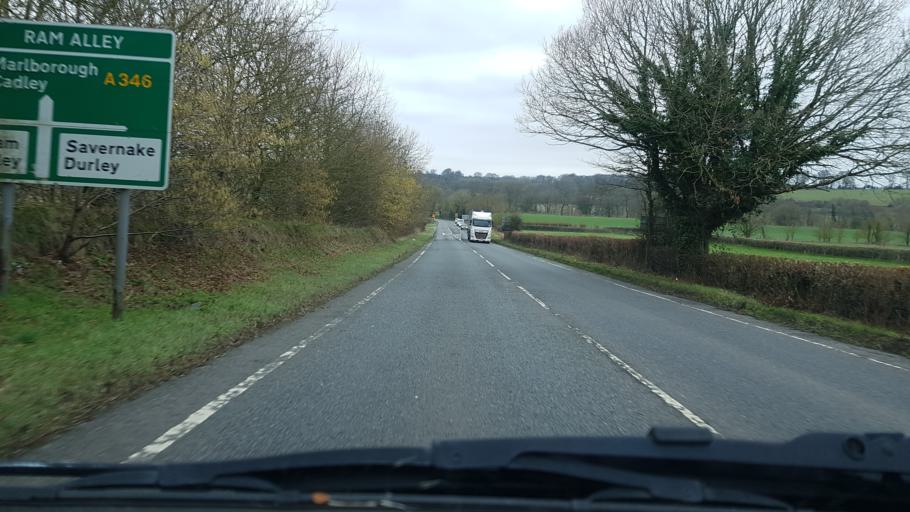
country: GB
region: England
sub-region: Wiltshire
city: Burbage
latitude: 51.3658
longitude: -1.6771
